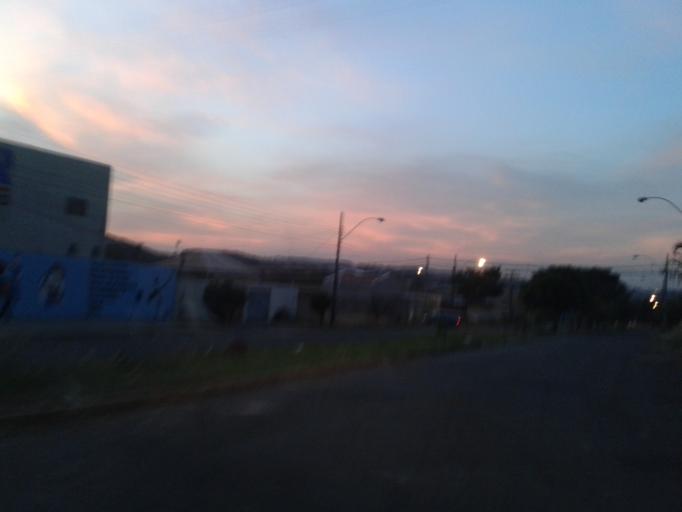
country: BR
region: Goias
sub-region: Goiania
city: Goiania
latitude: -16.6591
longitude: -49.3539
